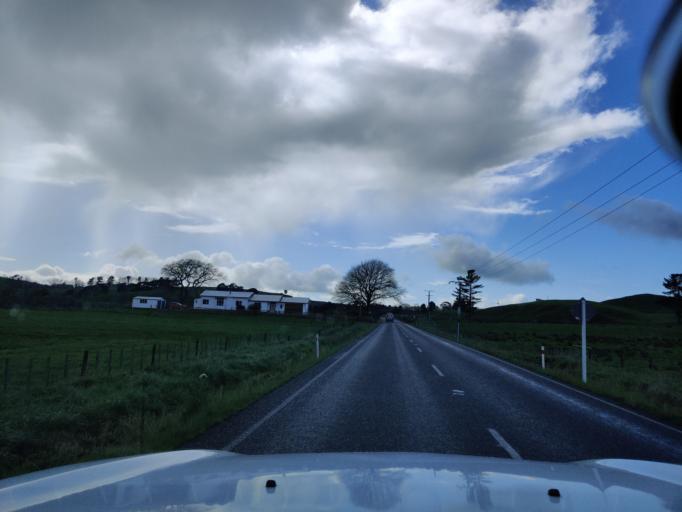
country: NZ
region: Waikato
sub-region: Waikato District
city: Ngaruawahia
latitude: -37.5794
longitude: 175.2233
